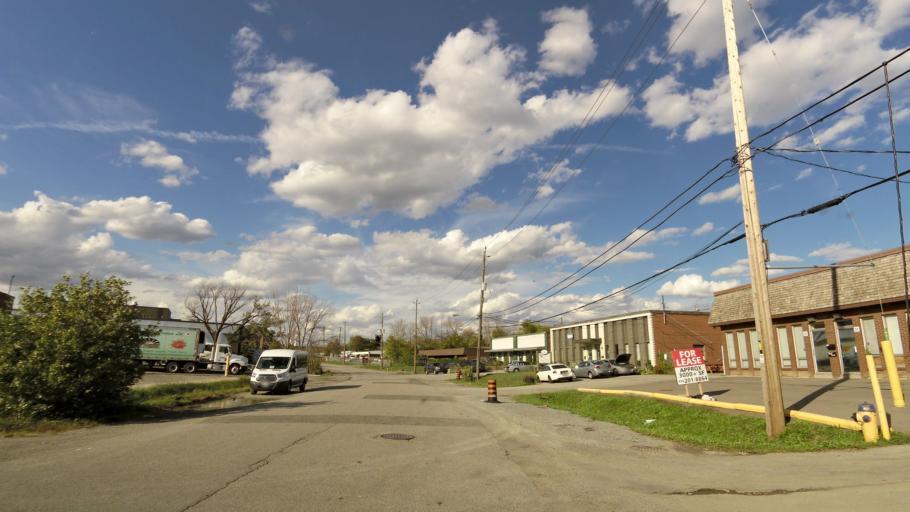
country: CA
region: Ontario
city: Etobicoke
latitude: 43.6037
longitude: -79.5262
